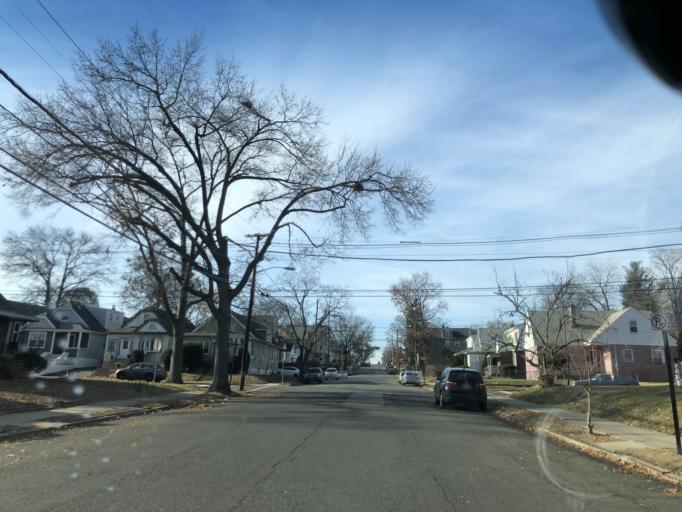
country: US
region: New Jersey
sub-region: Bergen County
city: Fair Lawn
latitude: 40.9260
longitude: -74.1441
